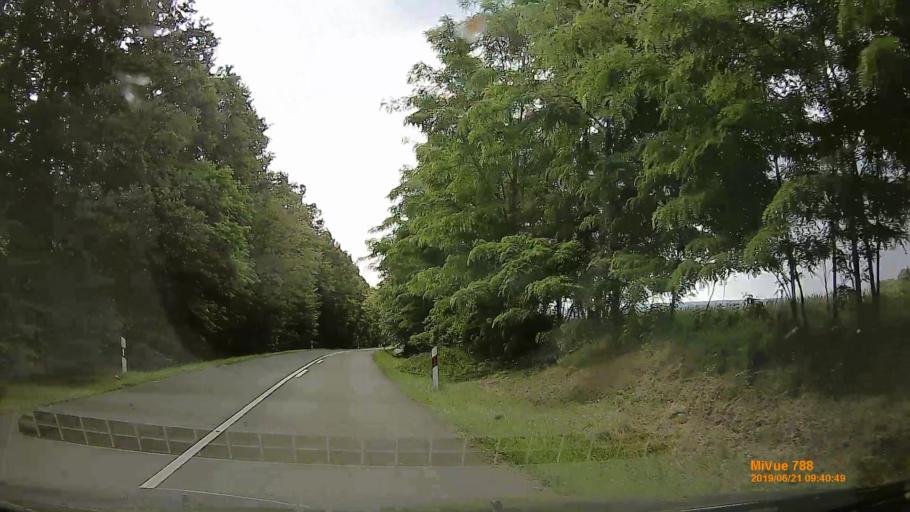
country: HU
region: Somogy
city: Taszar
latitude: 46.2940
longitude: 17.9485
